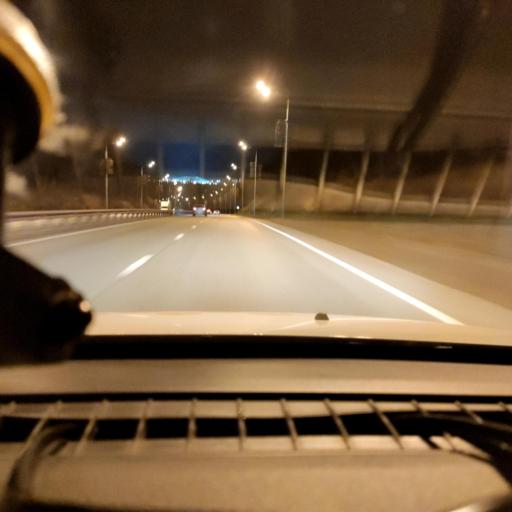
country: RU
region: Samara
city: Novosemeykino
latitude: 53.3174
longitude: 50.2300
